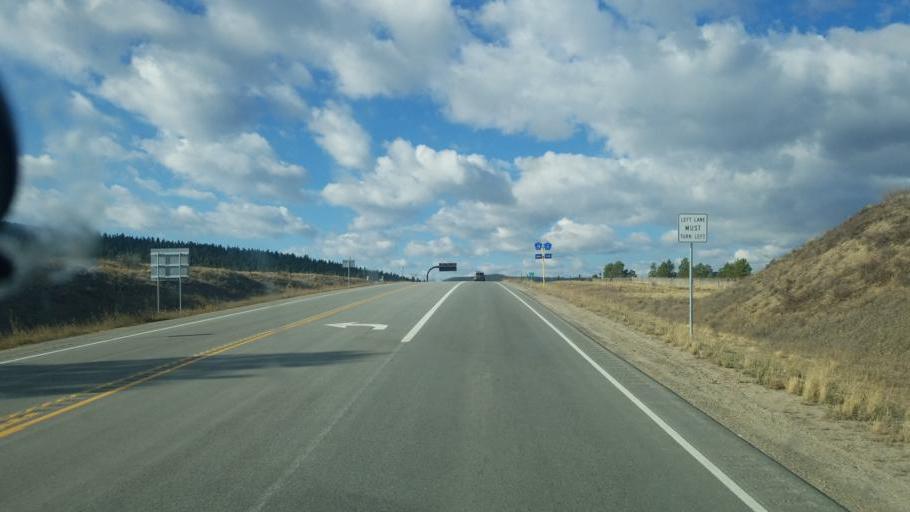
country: US
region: Colorado
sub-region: Chaffee County
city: Buena Vista
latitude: 38.9107
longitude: -105.9743
